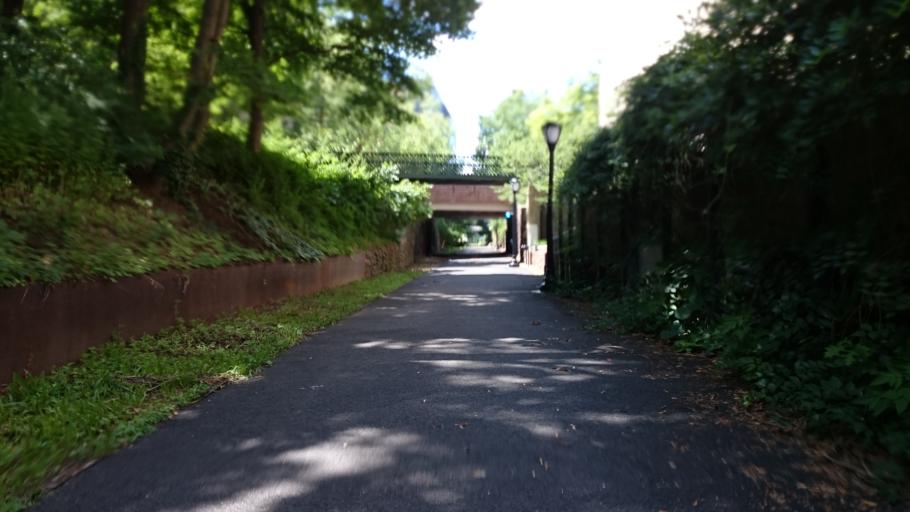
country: US
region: Connecticut
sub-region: New Haven County
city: New Haven
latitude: 41.3123
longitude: -72.9234
